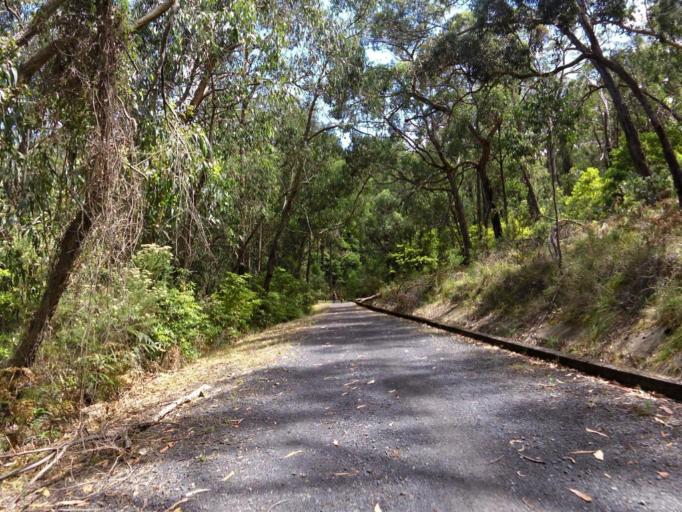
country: AU
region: Victoria
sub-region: Cardinia
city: Officer
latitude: -38.0350
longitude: 145.4421
